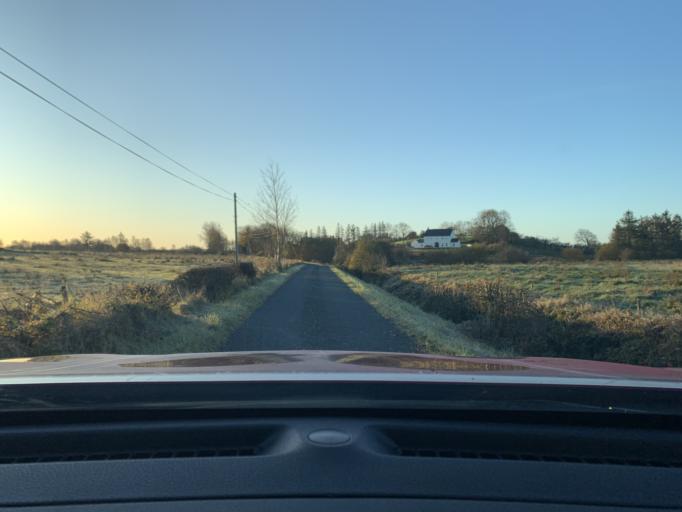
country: IE
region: Connaught
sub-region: Sligo
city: Ballymote
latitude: 54.0844
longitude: -8.5486
